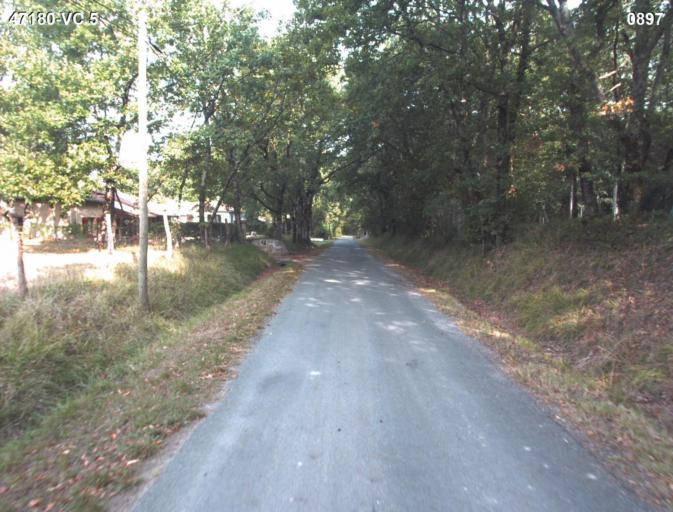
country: FR
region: Aquitaine
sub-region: Departement du Lot-et-Garonne
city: Sainte-Colombe-en-Bruilhois
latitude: 44.1750
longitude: 0.4686
